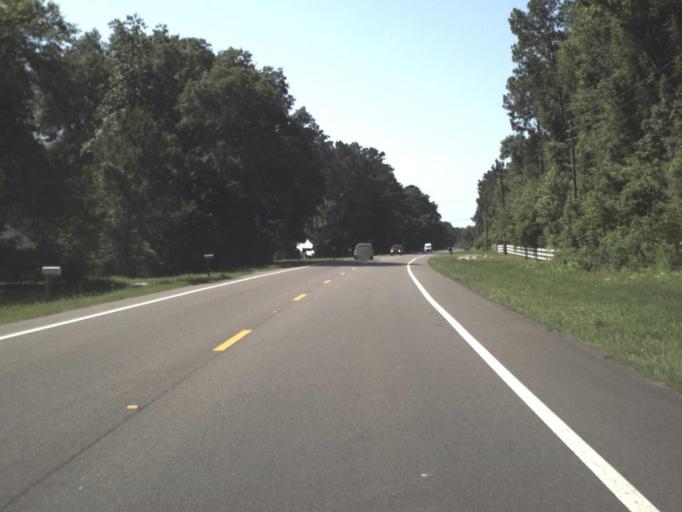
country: US
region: Florida
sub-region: Nassau County
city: Nassau Village-Ratliff
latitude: 30.5298
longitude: -81.7711
